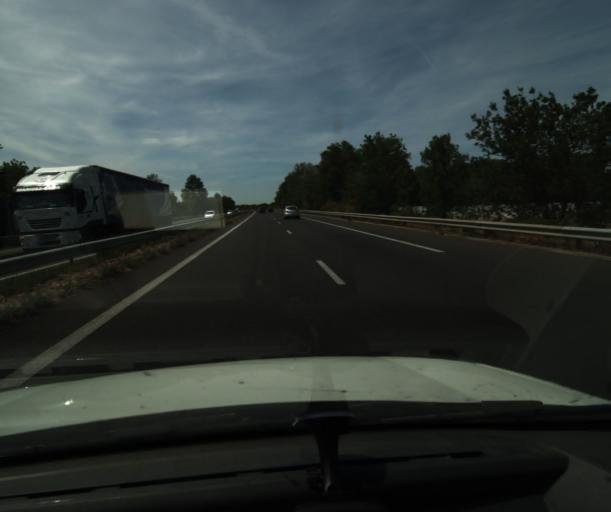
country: FR
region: Languedoc-Roussillon
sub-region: Departement de l'Aude
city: Villeneuve-la-Comptal
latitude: 43.3019
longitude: 1.9207
